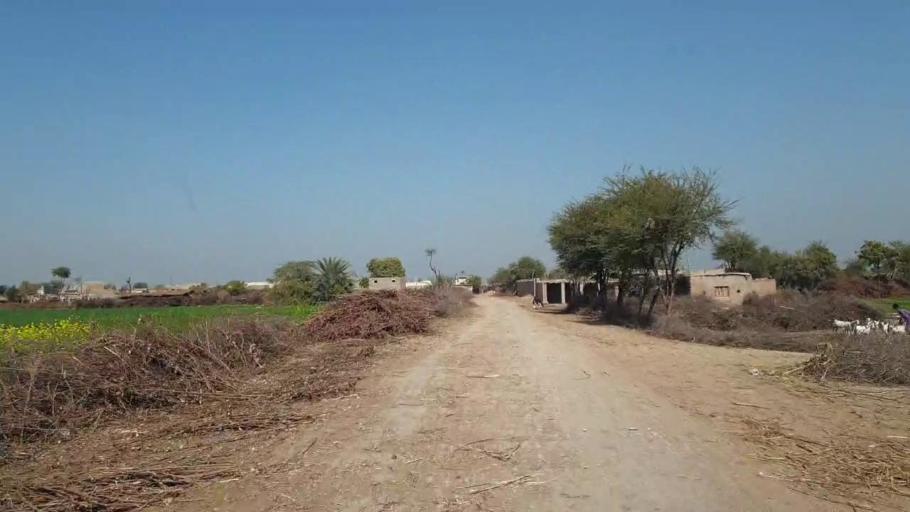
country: PK
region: Sindh
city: Shahdadpur
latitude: 25.9508
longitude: 68.5112
